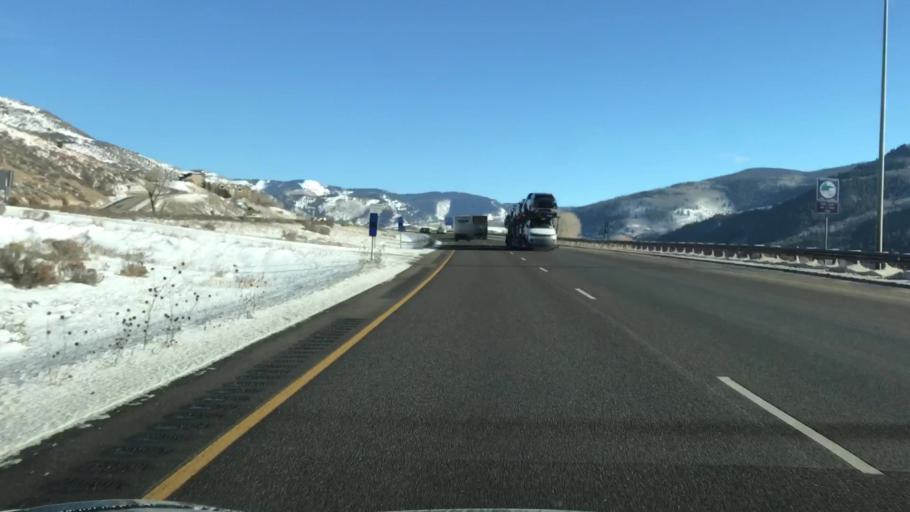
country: US
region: Colorado
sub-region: Eagle County
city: Avon
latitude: 39.6346
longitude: -106.5165
